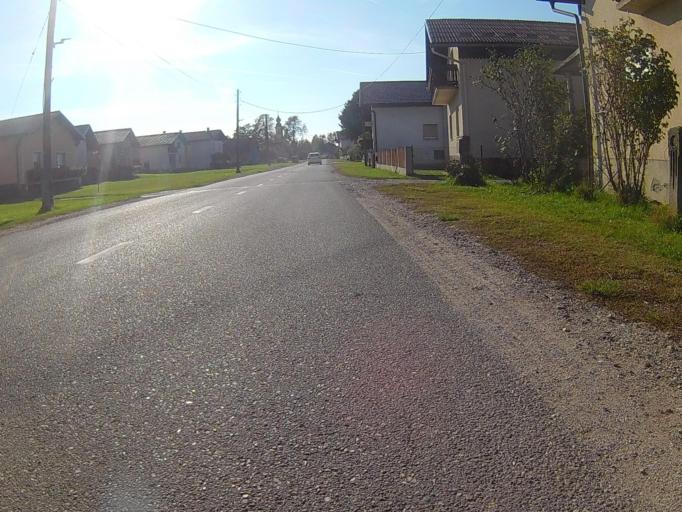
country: SI
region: Starse
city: Starse
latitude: 46.4450
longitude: 15.7635
